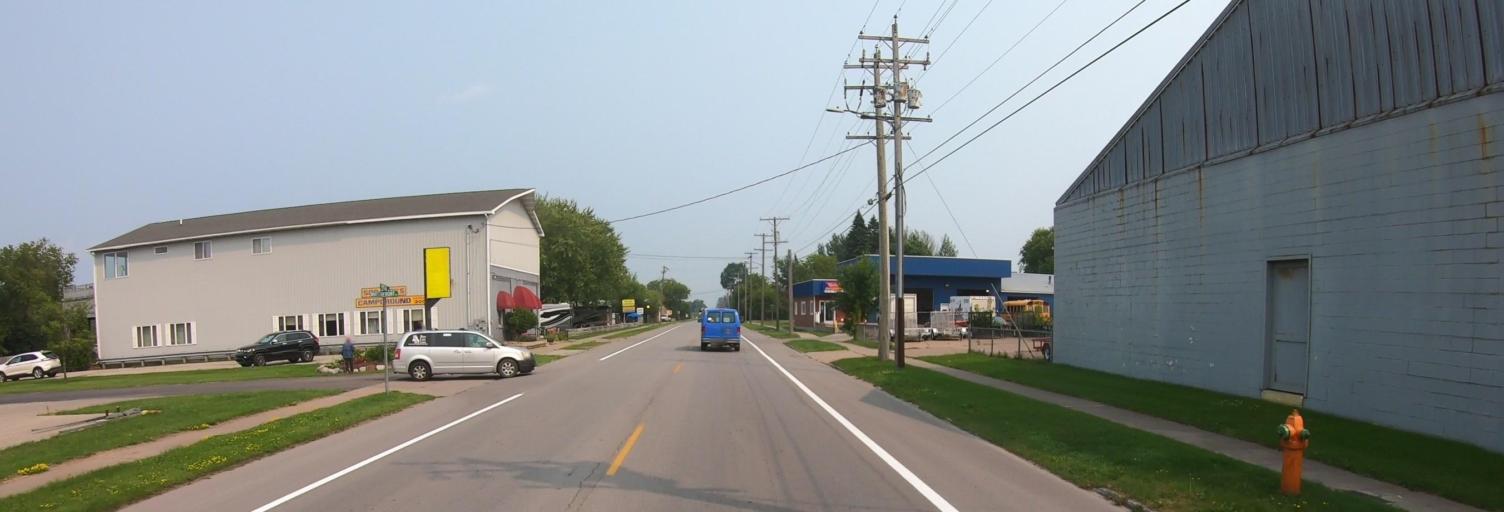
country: US
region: Michigan
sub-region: Chippewa County
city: Sault Ste. Marie
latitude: 46.4934
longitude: -84.3255
